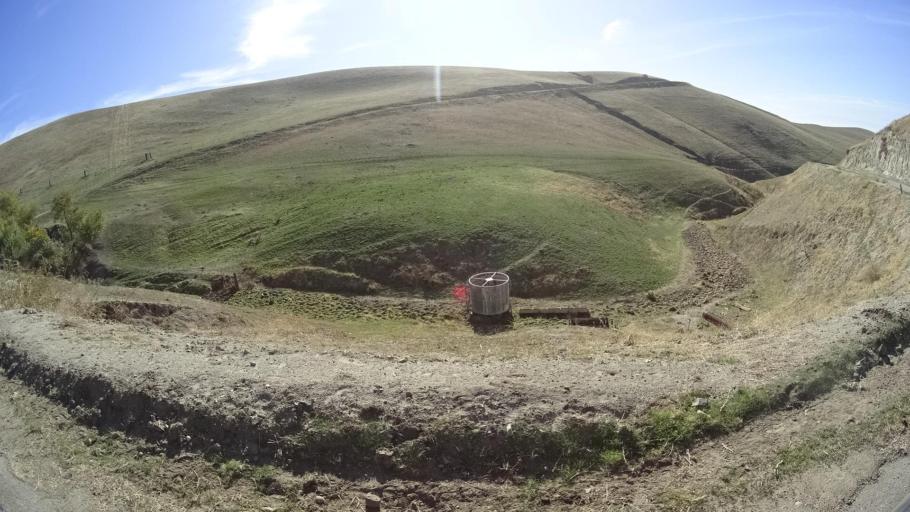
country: US
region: California
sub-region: Kern County
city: Arvin
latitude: 35.4119
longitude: -118.7613
